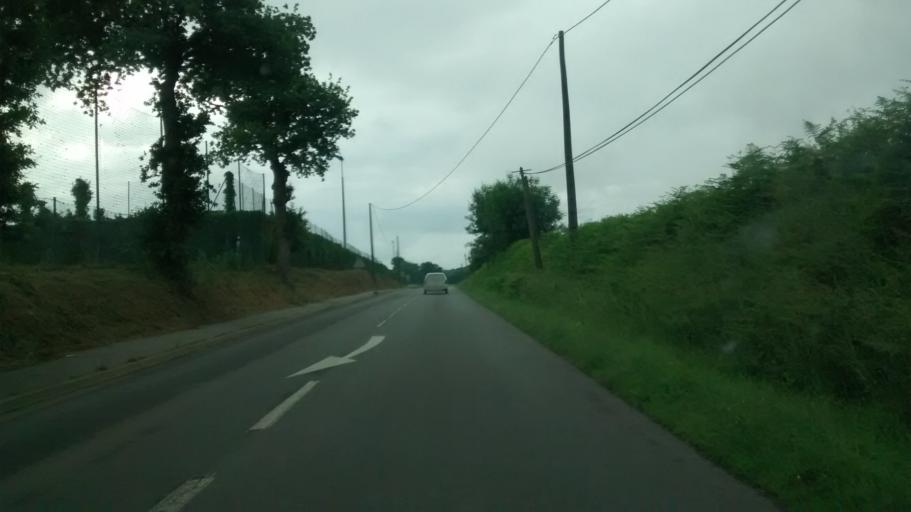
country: FR
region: Brittany
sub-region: Departement du Morbihan
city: Serent
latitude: 47.8216
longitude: -2.4997
